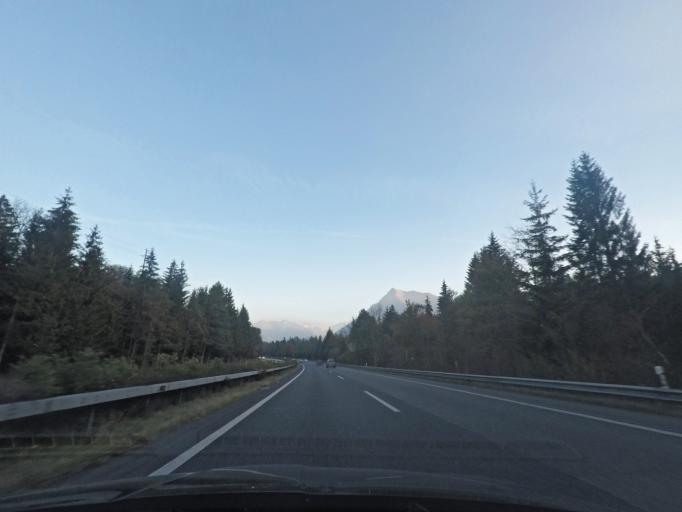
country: CH
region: Bern
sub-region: Thun District
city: Thun
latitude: 46.7191
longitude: 7.6107
